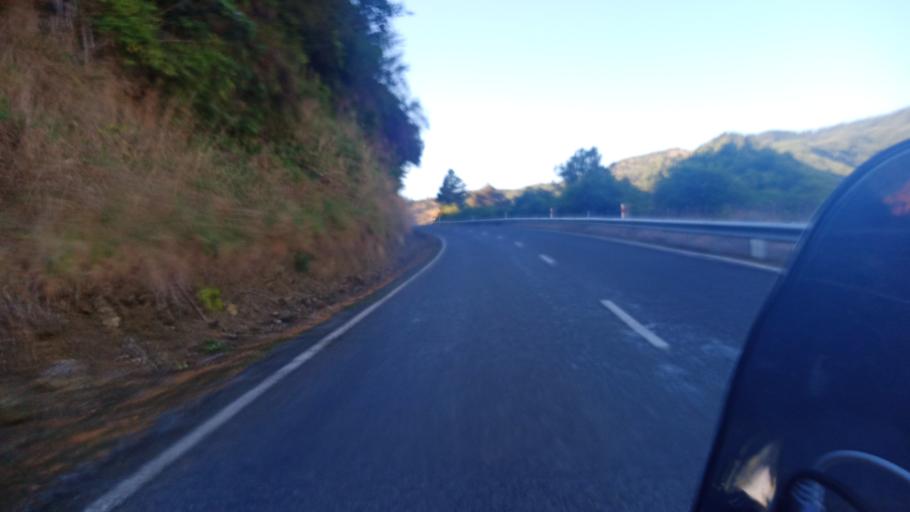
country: NZ
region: Hawke's Bay
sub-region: Wairoa District
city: Wairoa
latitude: -38.8771
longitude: 177.2245
